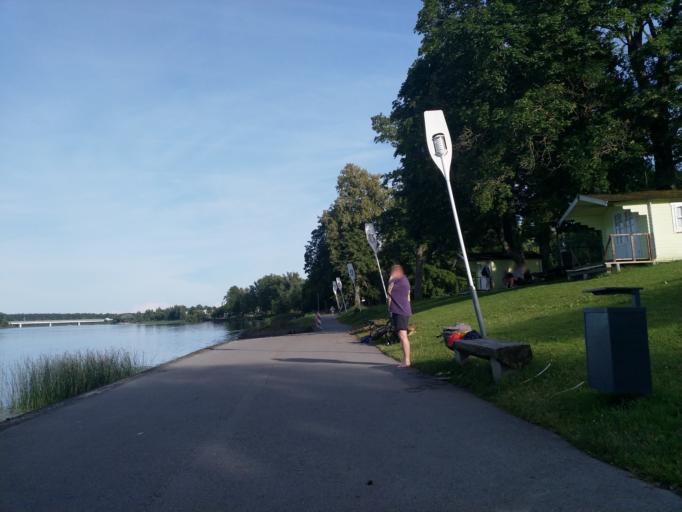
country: EE
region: Paernumaa
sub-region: Paernu linn
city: Parnu
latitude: 58.3804
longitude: 24.5363
